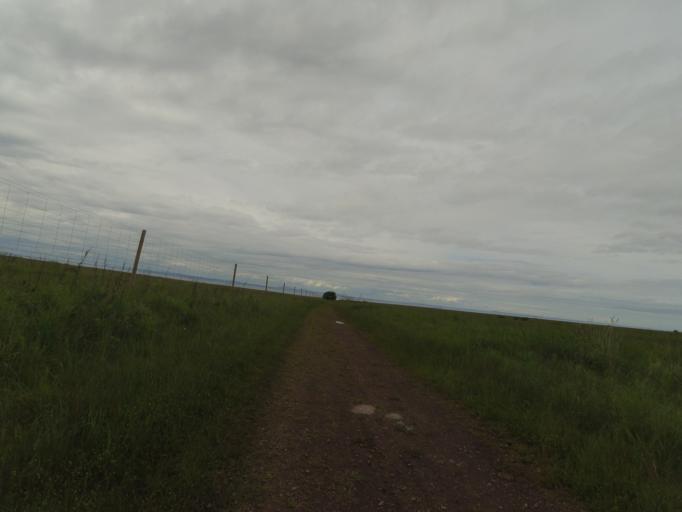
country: GB
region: Scotland
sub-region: East Lothian
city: Macmerry
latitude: 55.9528
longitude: -2.9255
